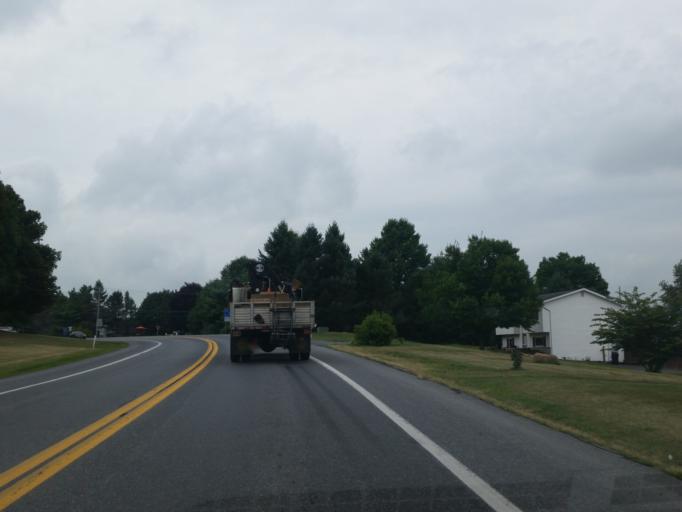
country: US
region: Pennsylvania
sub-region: Lancaster County
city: Lititz
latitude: 40.1909
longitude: -76.3093
